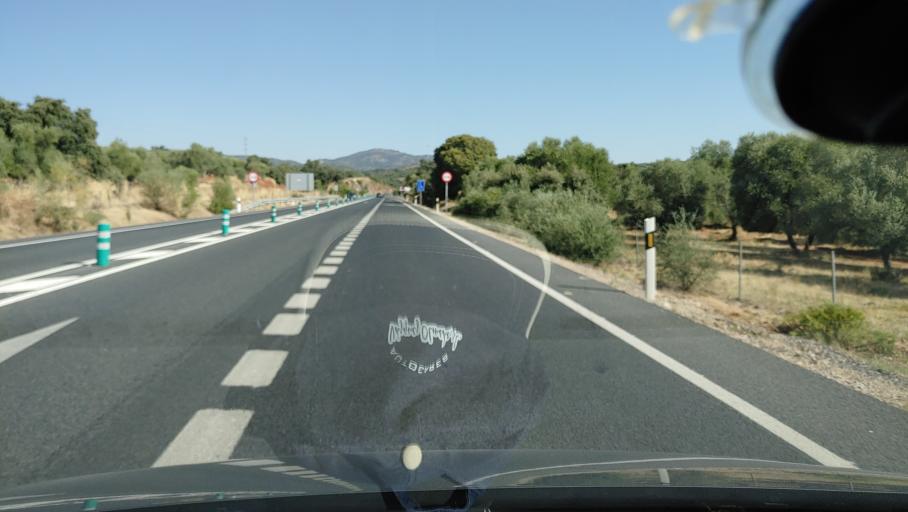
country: ES
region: Andalusia
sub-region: Province of Cordoba
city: Cordoba
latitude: 37.9234
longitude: -4.7654
